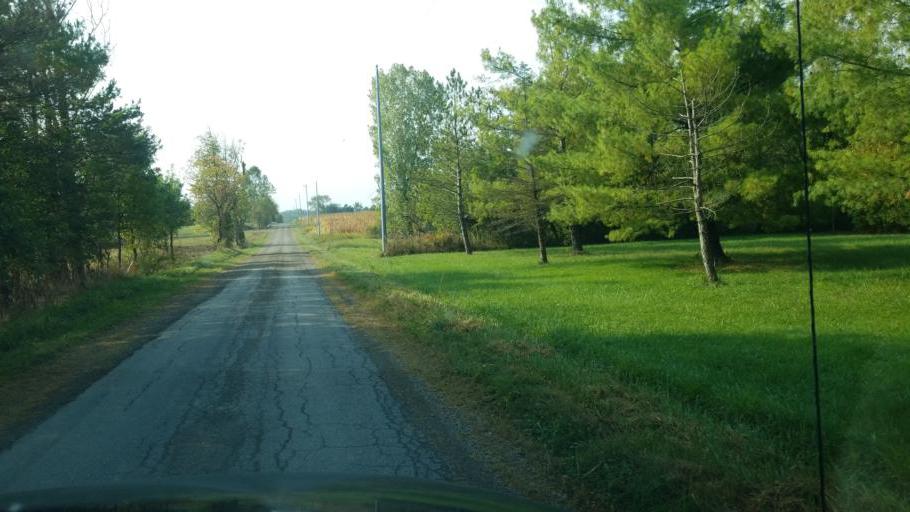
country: US
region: Ohio
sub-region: Knox County
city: Centerburg
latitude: 40.2821
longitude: -82.5875
